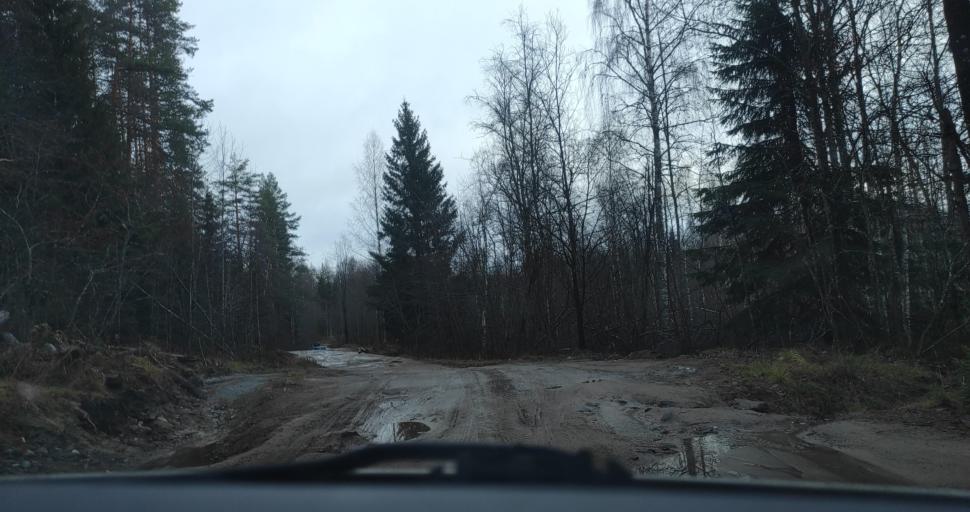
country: RU
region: Republic of Karelia
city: Pitkyaranta
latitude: 61.7459
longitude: 31.3955
